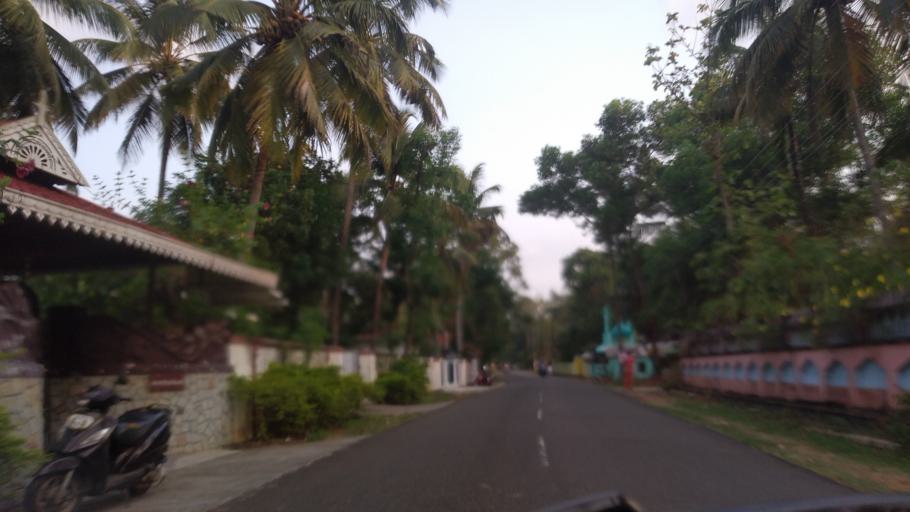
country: IN
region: Kerala
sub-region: Thrissur District
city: Thanniyam
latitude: 10.3328
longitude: 76.1206
